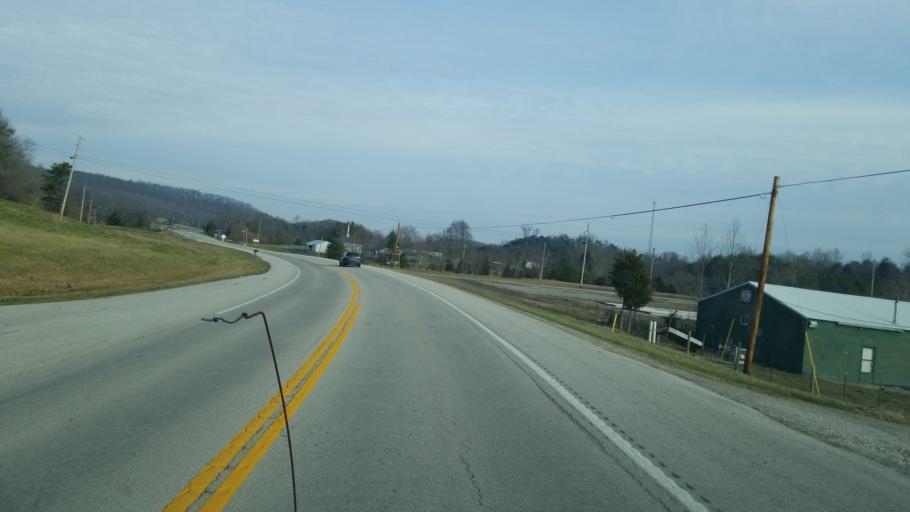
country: US
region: Kentucky
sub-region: Russell County
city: Russell Springs
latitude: 37.1682
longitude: -85.0068
